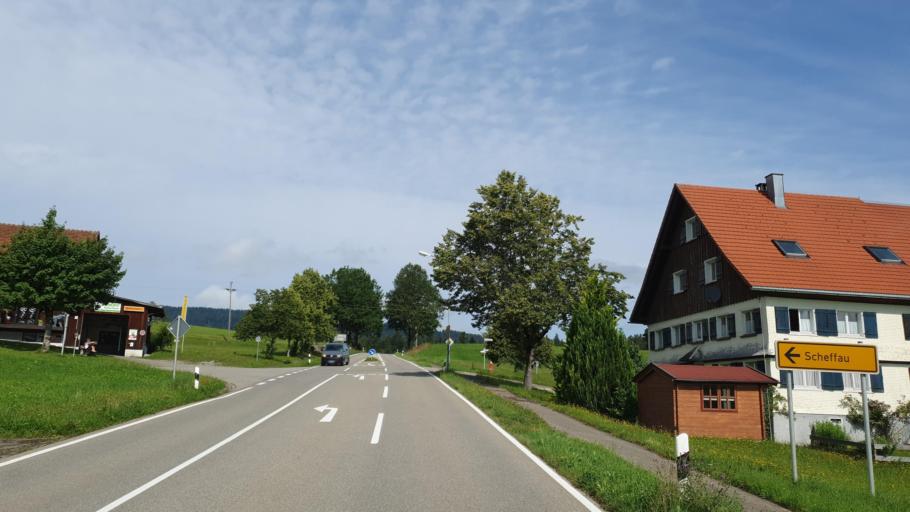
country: AT
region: Vorarlberg
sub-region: Politischer Bezirk Bregenz
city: Sulzberg
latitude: 47.5420
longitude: 9.8660
